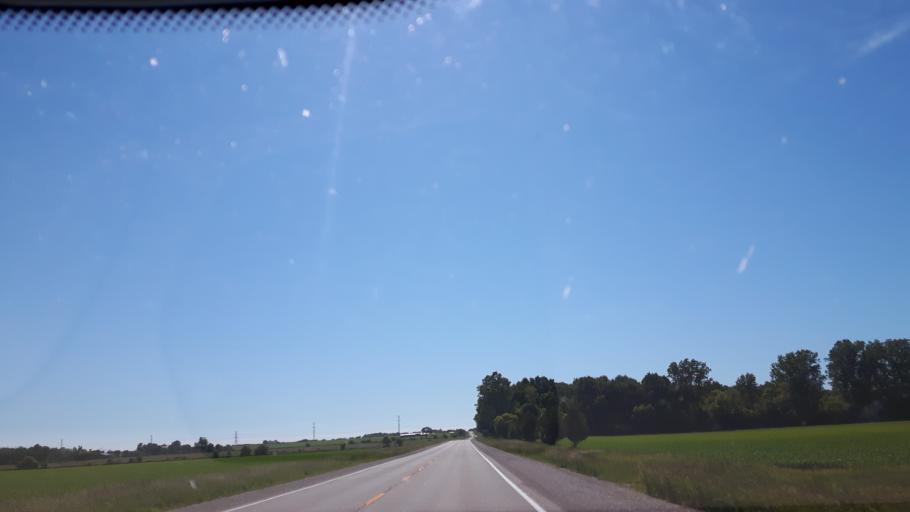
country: CA
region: Ontario
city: Bluewater
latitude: 43.4255
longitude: -81.5830
